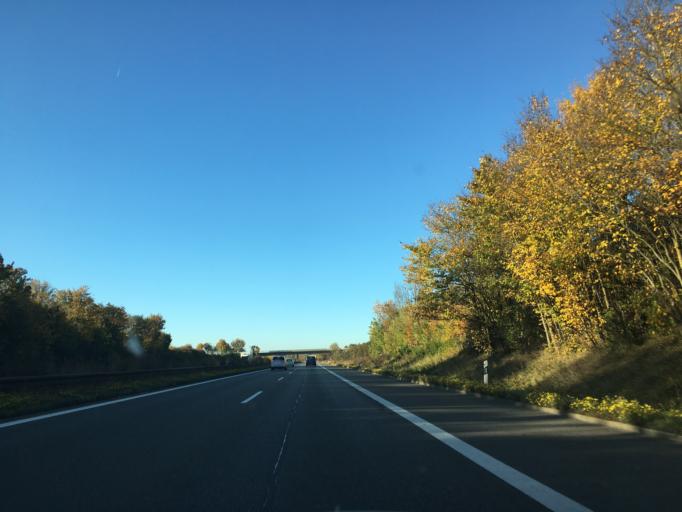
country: DE
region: Baden-Wuerttemberg
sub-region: Freiburg Region
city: Deisslingen
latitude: 48.1096
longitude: 8.5828
